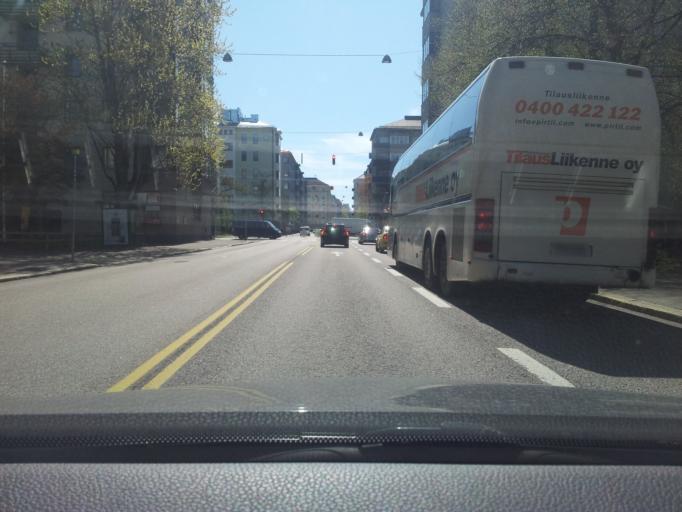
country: FI
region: Uusimaa
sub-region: Helsinki
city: Helsinki
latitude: 60.1860
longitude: 24.9157
